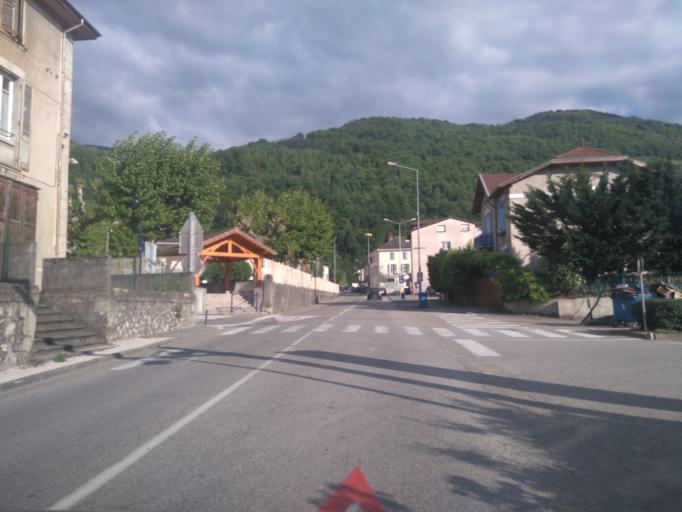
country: FR
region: Rhone-Alpes
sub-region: Departement de l'Isere
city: Villard-Bonnot
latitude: 45.2349
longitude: 5.8816
